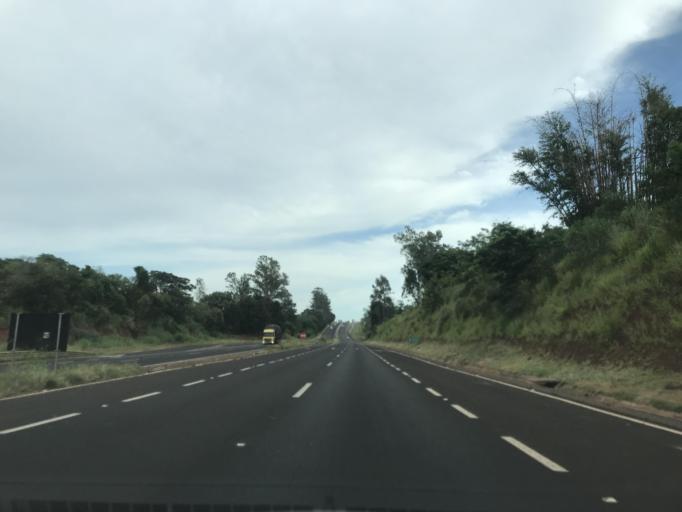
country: BR
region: Parana
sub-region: Alto Parana
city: Alto Parana
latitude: -23.1395
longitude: -52.2876
